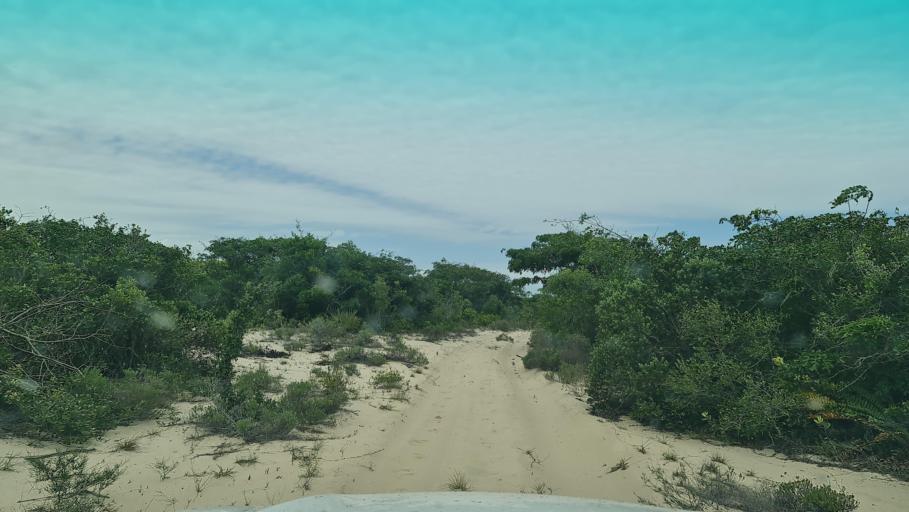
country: MZ
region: Maputo
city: Manhica
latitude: -25.6338
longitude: 32.7858
